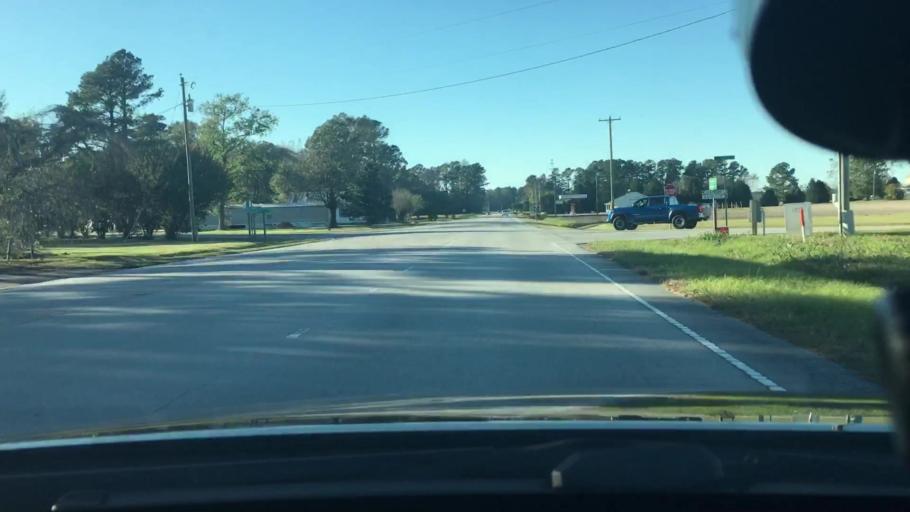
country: US
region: North Carolina
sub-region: Craven County
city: Vanceboro
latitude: 35.3776
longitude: -77.2165
